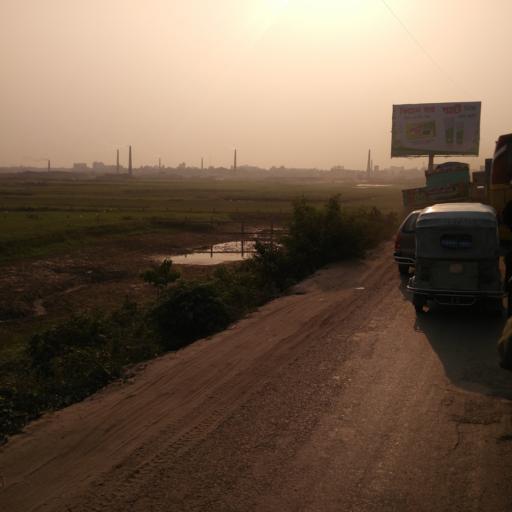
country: BD
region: Dhaka
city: Tungi
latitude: 23.8951
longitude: 90.3451
